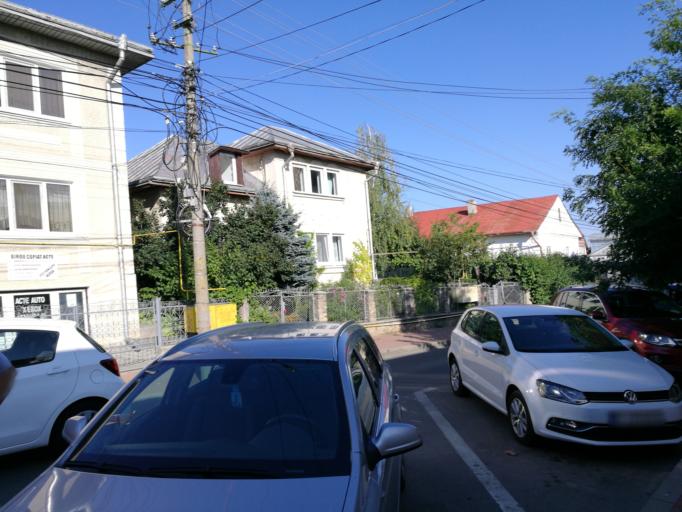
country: RO
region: Suceava
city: Suceava
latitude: 47.6500
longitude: 26.2557
